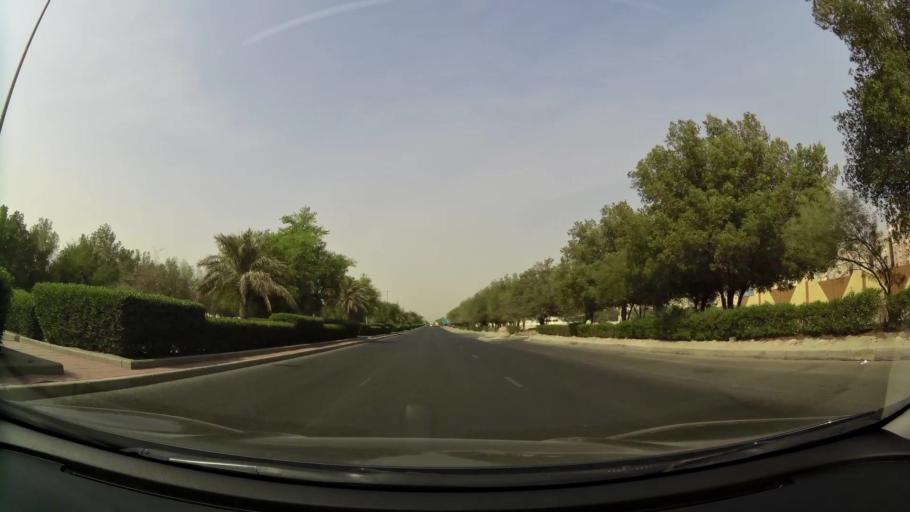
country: KW
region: Al Farwaniyah
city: Al Farwaniyah
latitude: 29.2504
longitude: 47.9259
